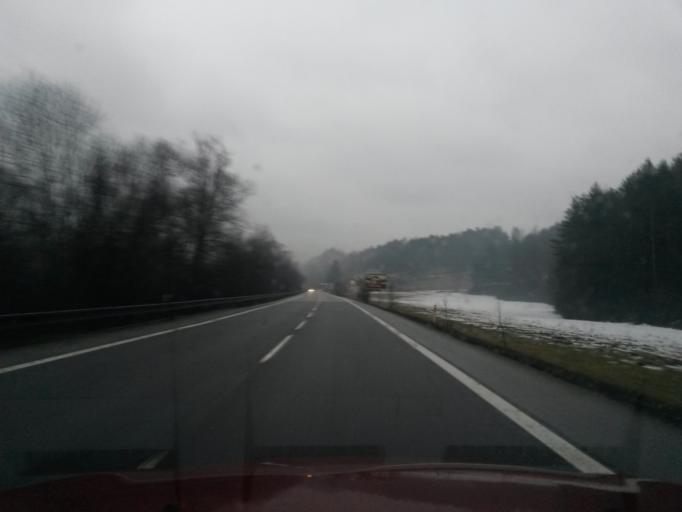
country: SK
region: Zilinsky
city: Kysucke Nove Mesto
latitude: 49.2850
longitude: 18.7770
